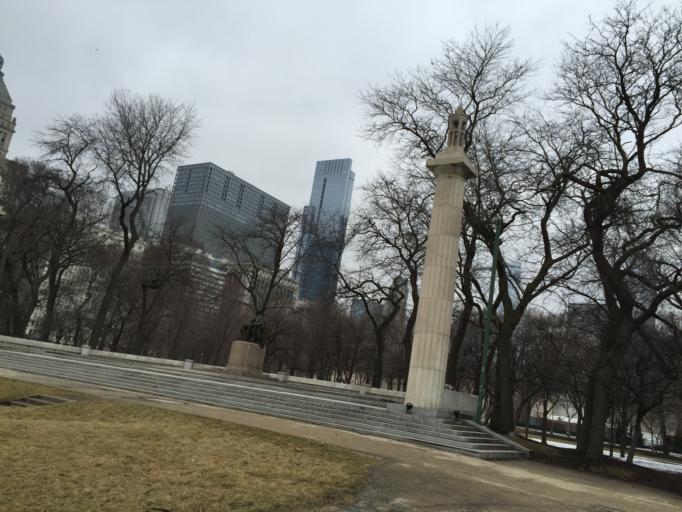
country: US
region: Illinois
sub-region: Cook County
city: Chicago
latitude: 41.8770
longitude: -87.6212
